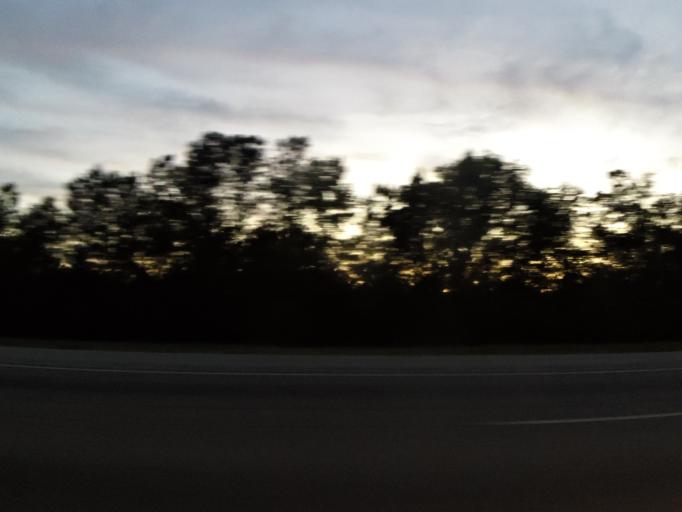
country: US
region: Georgia
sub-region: Liberty County
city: Midway
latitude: 31.7255
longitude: -81.3891
